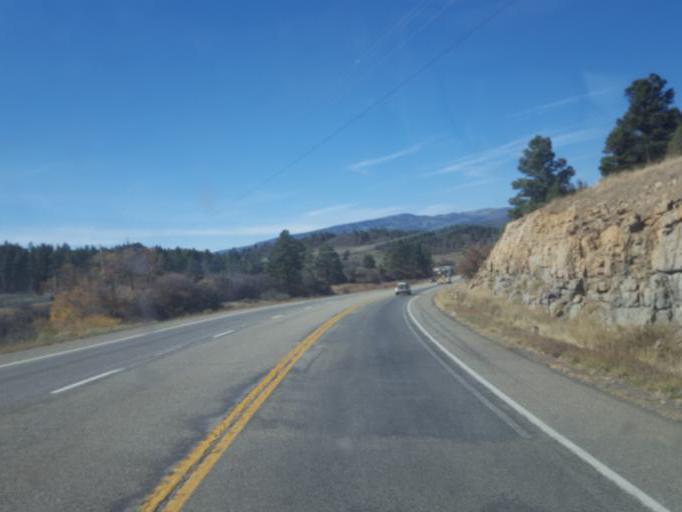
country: US
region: Colorado
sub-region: Archuleta County
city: Pagosa Springs
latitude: 37.2274
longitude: -107.1181
